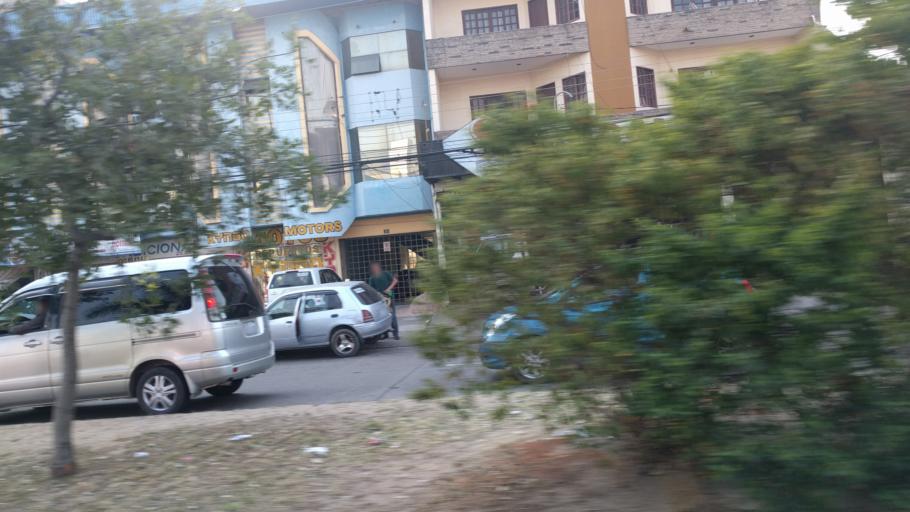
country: BO
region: Santa Cruz
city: Santa Cruz de la Sierra
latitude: -17.7840
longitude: -63.1645
